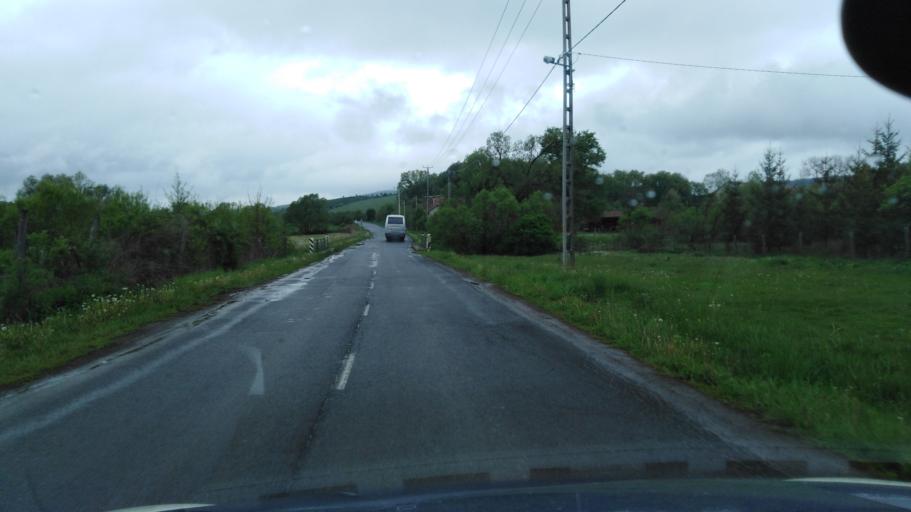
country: HU
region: Nograd
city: Rimoc
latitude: 47.9974
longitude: 19.6199
